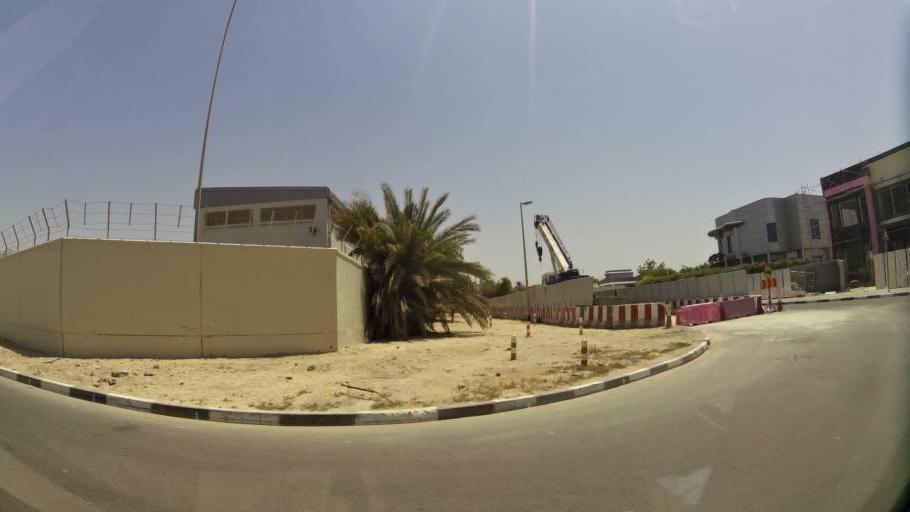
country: AE
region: Ash Shariqah
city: Sharjah
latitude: 25.2957
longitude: 55.3437
